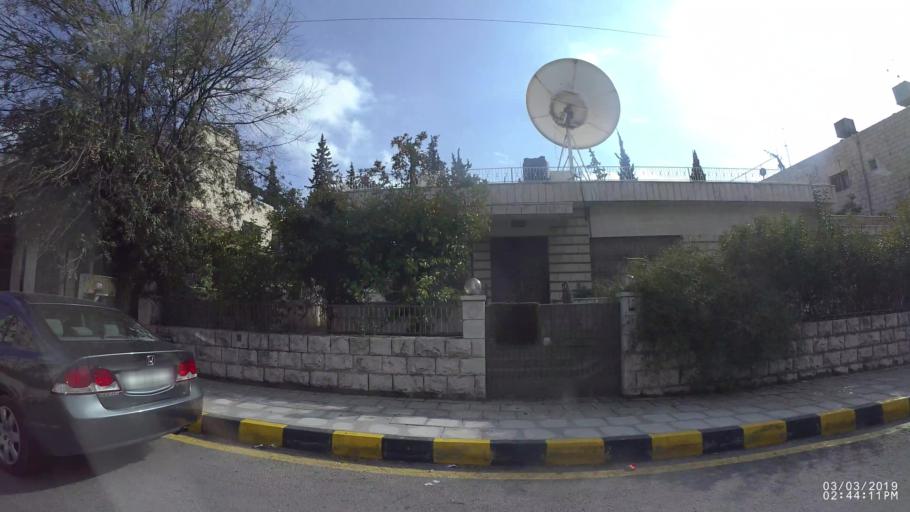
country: JO
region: Amman
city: Amman
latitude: 31.9659
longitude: 35.8912
